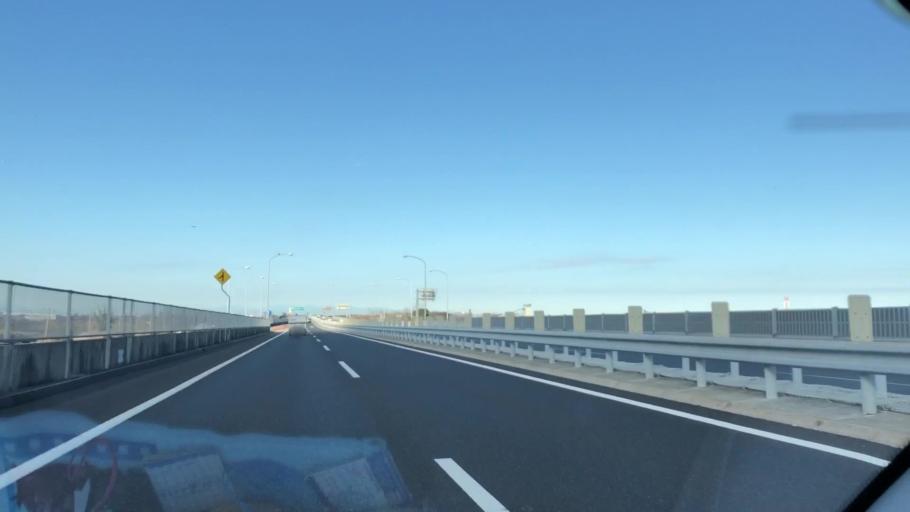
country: JP
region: Chiba
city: Kisarazu
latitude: 35.4150
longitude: 139.9511
